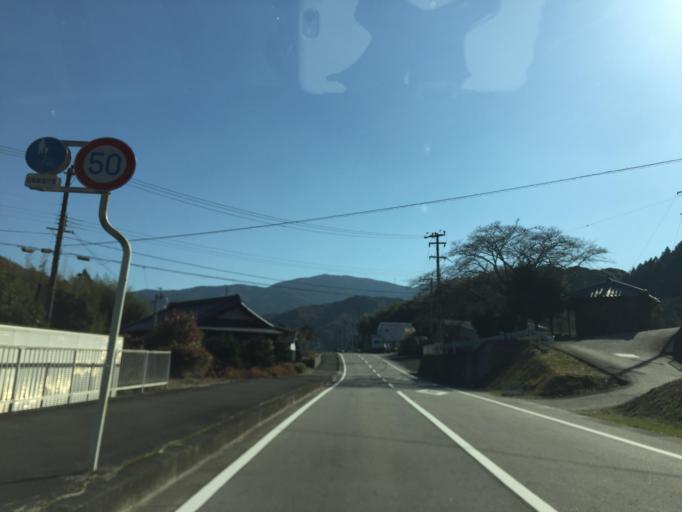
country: JP
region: Wakayama
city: Iwade
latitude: 34.1527
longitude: 135.3440
